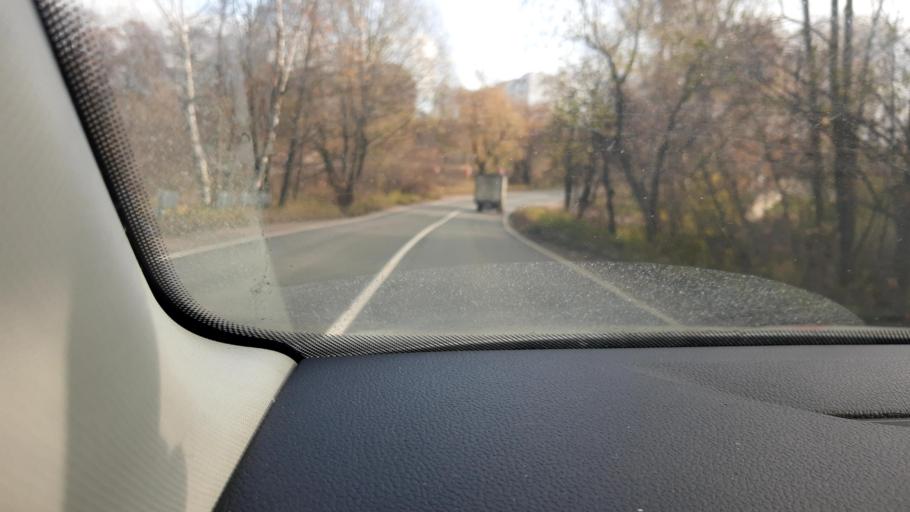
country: RU
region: Moskovskaya
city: Shcherbinka
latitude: 55.4709
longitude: 37.6054
